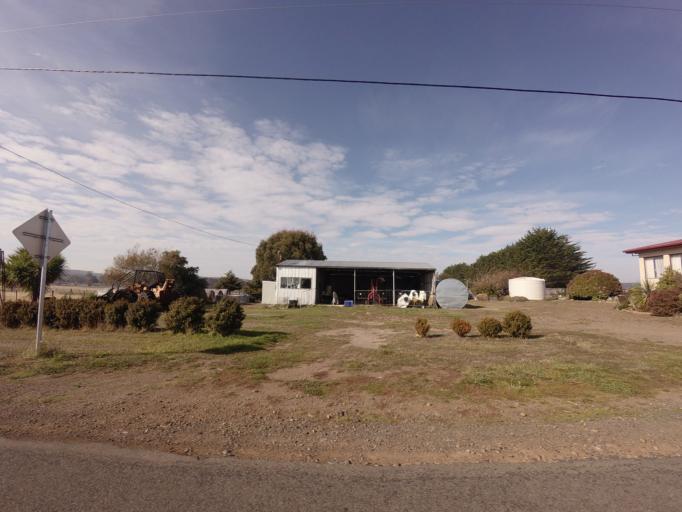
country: AU
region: Tasmania
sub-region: Sorell
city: Sorell
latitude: -42.4528
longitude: 147.4616
